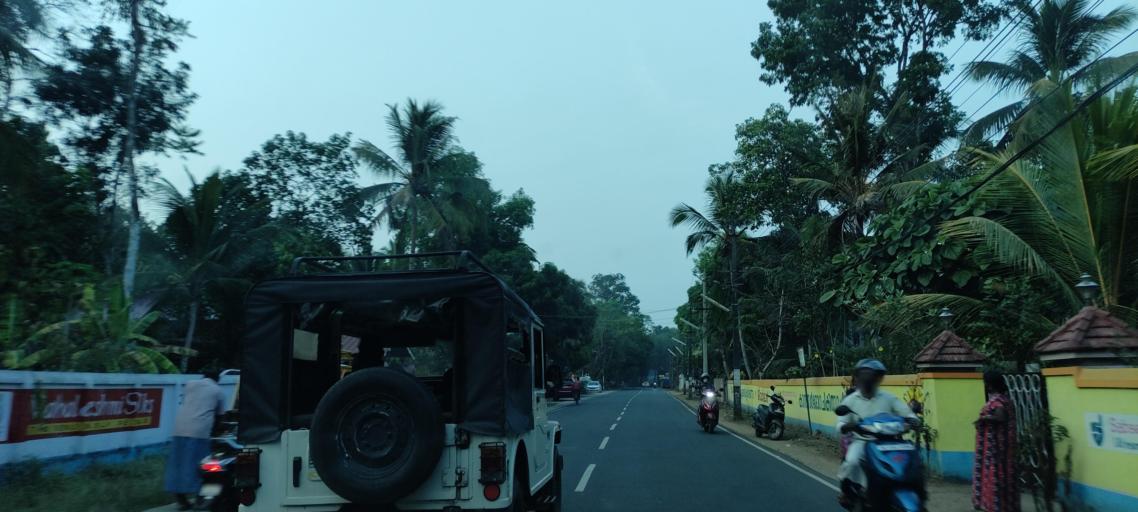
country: IN
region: Kerala
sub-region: Alappuzha
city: Mavelikara
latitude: 9.3000
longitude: 76.5336
